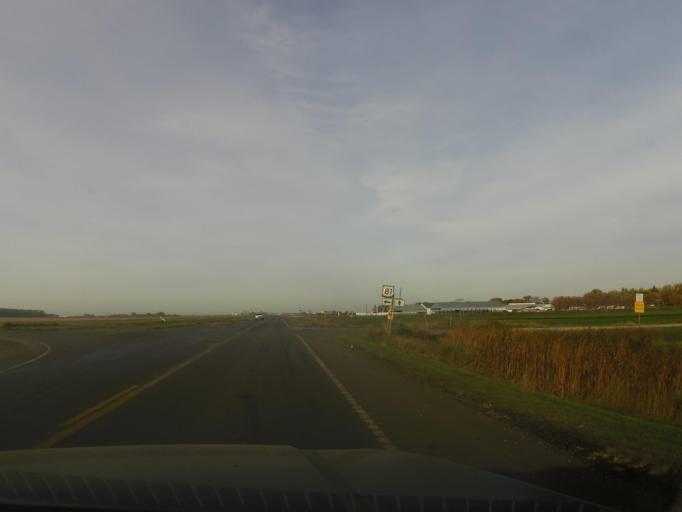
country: US
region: North Dakota
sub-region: Pembina County
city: Cavalier
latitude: 48.8044
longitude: -97.4466
